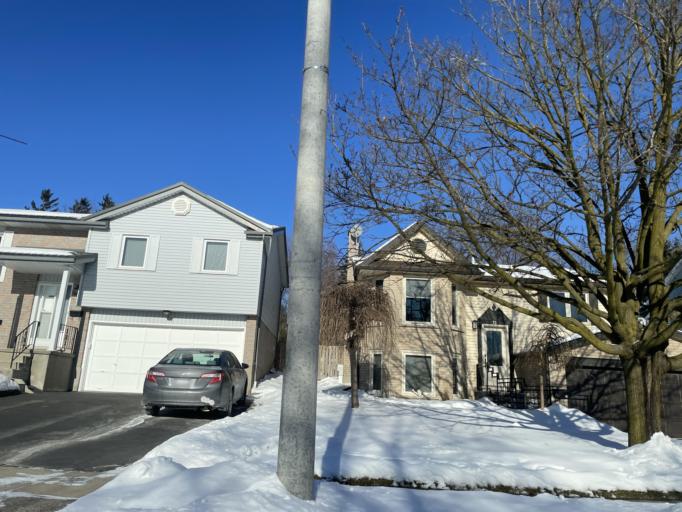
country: CA
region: Ontario
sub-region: Wellington County
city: Guelph
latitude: 43.5410
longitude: -80.2880
